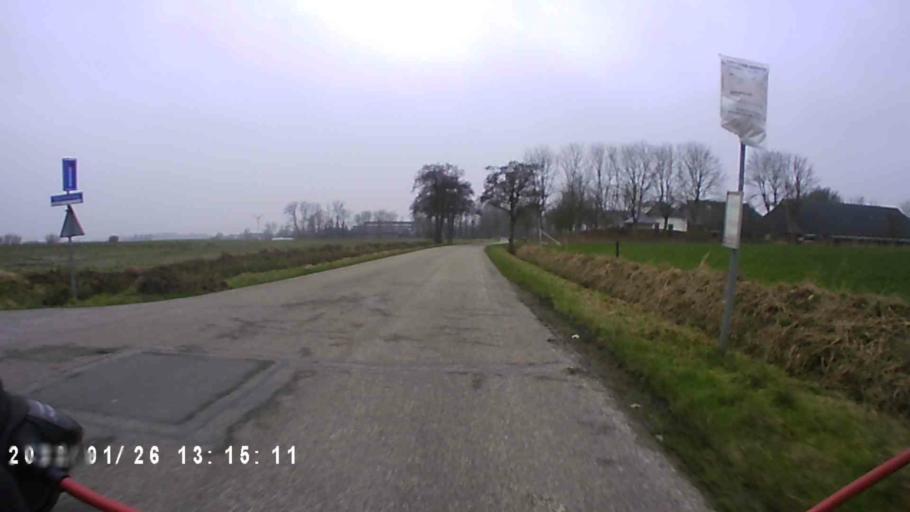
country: NL
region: Groningen
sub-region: Gemeente Zuidhorn
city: Oldehove
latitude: 53.3596
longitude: 6.3999
